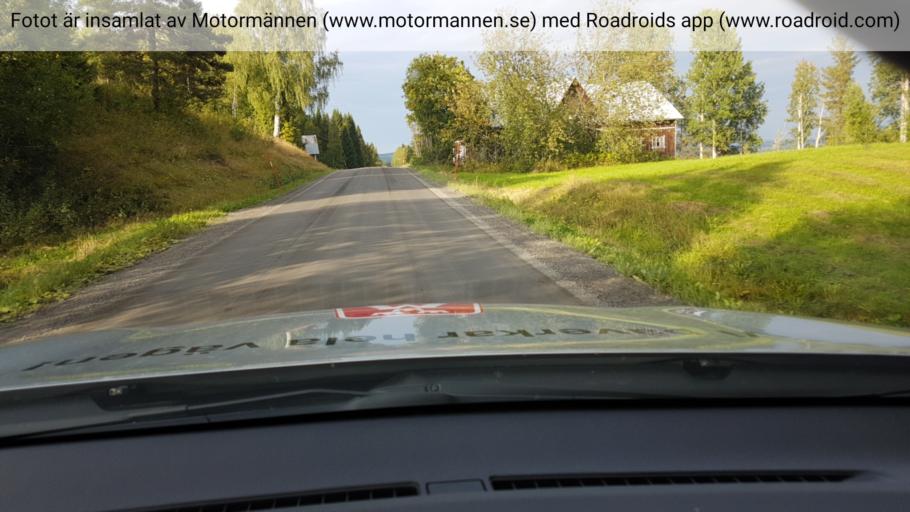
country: SE
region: Jaemtland
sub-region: Stroemsunds Kommun
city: Stroemsund
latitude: 64.0393
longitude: 15.8099
